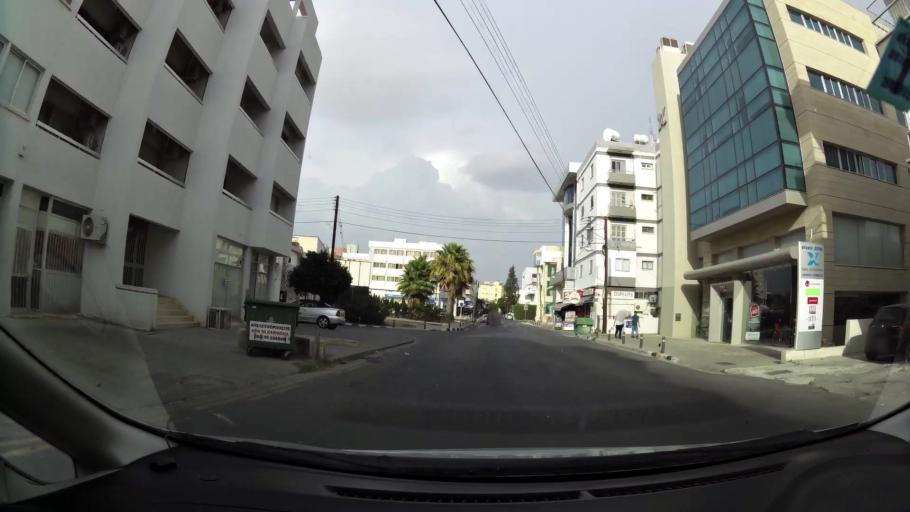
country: CY
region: Lefkosia
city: Nicosia
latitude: 35.1605
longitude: 33.3442
